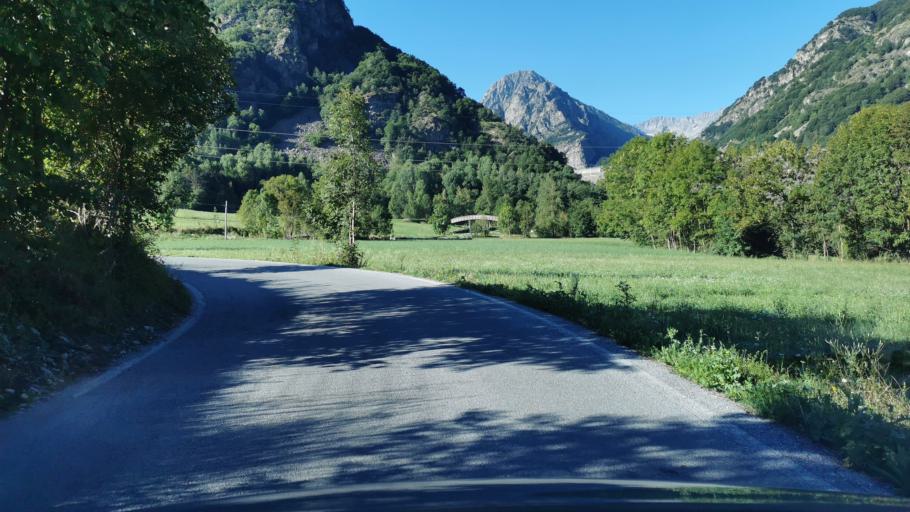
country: IT
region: Piedmont
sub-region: Provincia di Cuneo
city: Entracque
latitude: 44.2293
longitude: 7.3954
